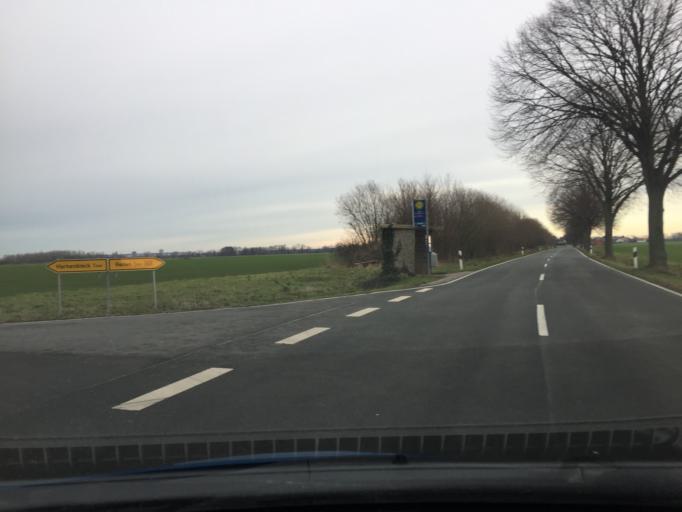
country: DE
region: Lower Saxony
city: Pattensen
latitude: 52.2793
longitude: 9.7661
